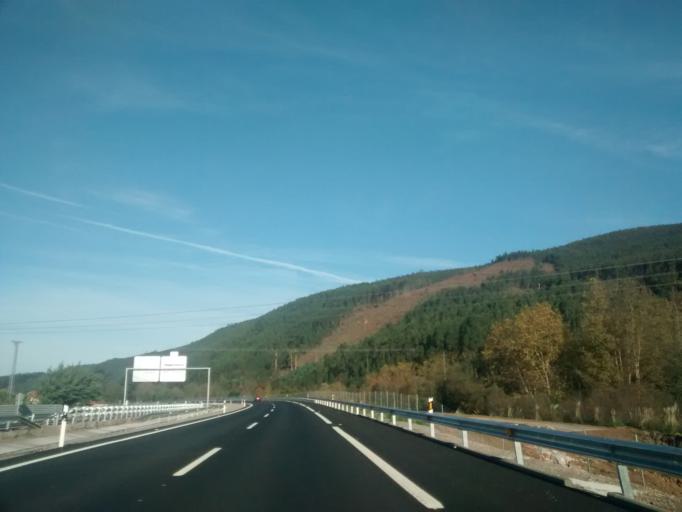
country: ES
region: Cantabria
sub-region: Provincia de Cantabria
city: Puente Viesgo
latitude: 43.3179
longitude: -3.9504
